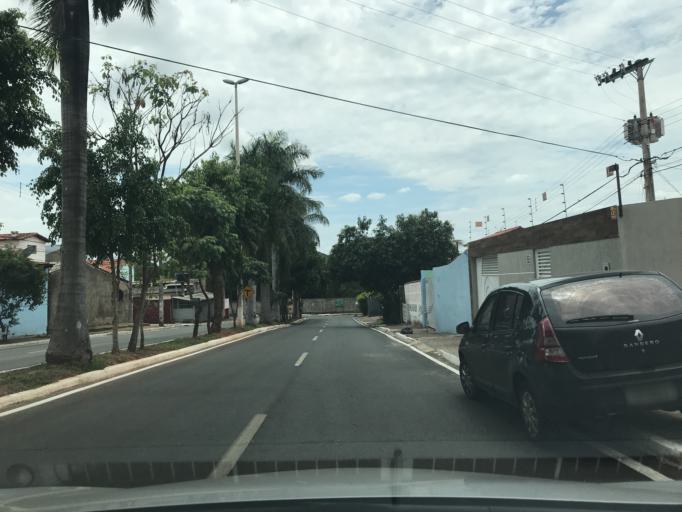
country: BR
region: Federal District
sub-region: Brasilia
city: Brasilia
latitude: -15.8520
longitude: -47.9460
